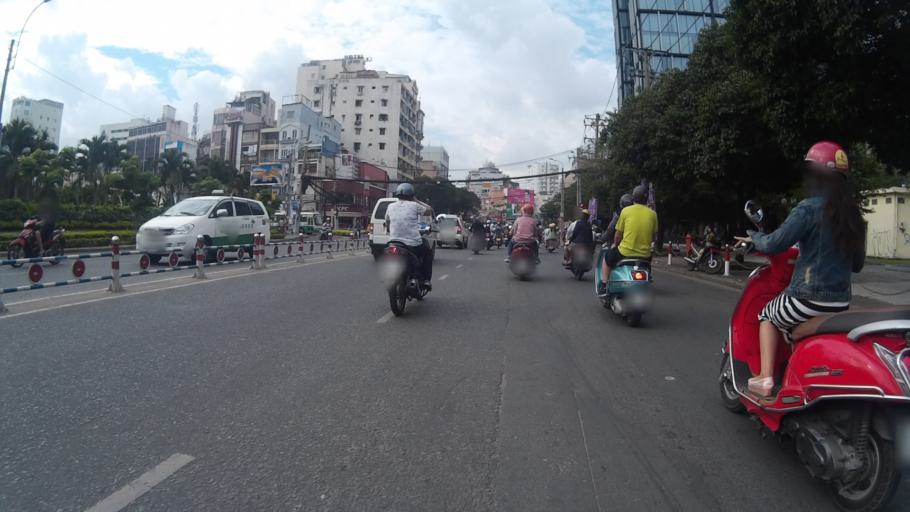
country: VN
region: Ho Chi Minh City
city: Quan Ba
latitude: 10.7697
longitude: 106.6945
